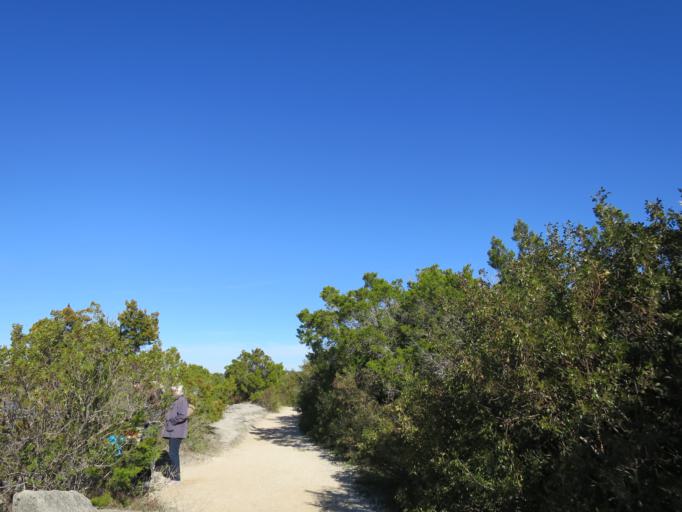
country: US
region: Texas
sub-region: Travis County
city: West Lake Hills
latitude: 30.3227
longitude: -97.7736
